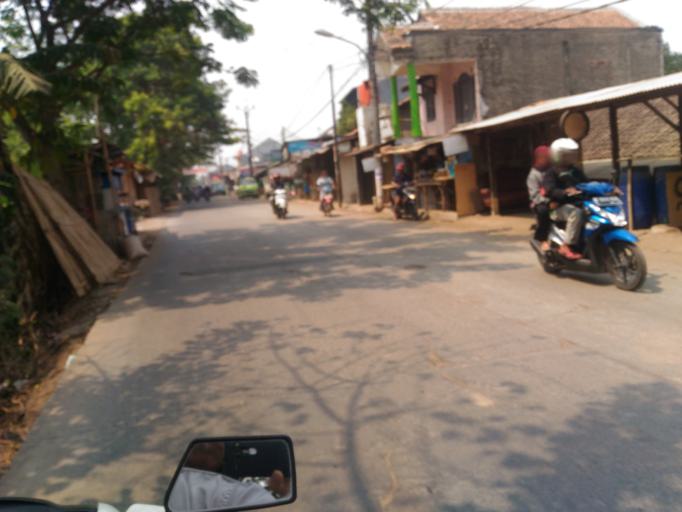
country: ID
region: West Java
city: Sepatan
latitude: -6.1469
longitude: 106.5679
